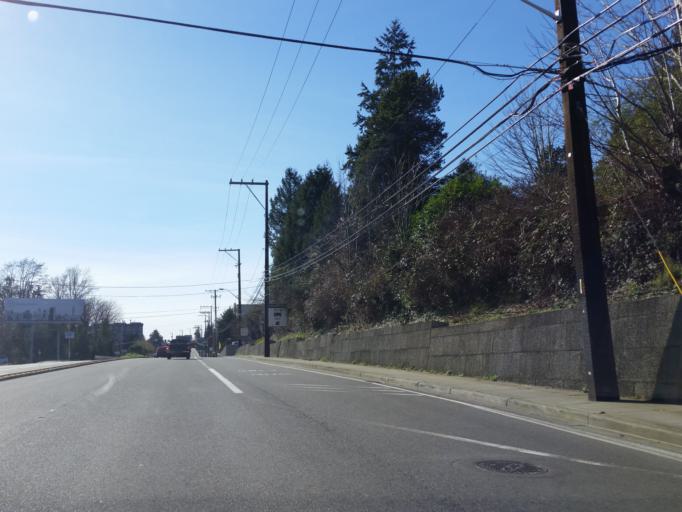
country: US
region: Washington
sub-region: King County
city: Lake Forest Park
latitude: 47.7420
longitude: -122.2878
